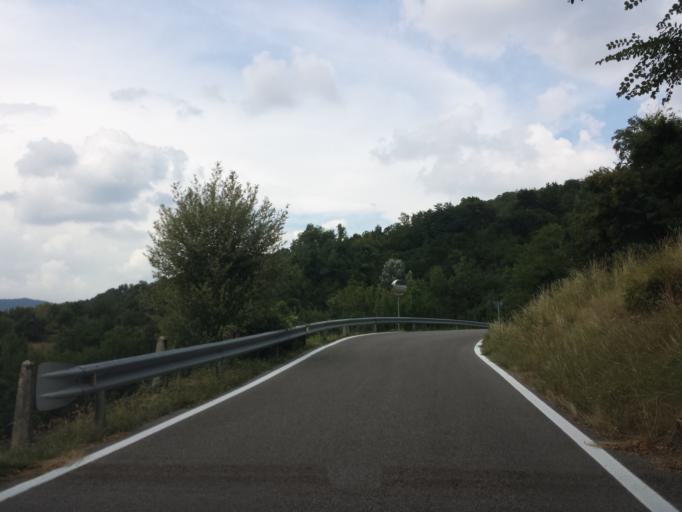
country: IT
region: Veneto
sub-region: Provincia di Vicenza
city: Valdagno
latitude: 45.6421
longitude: 11.3171
